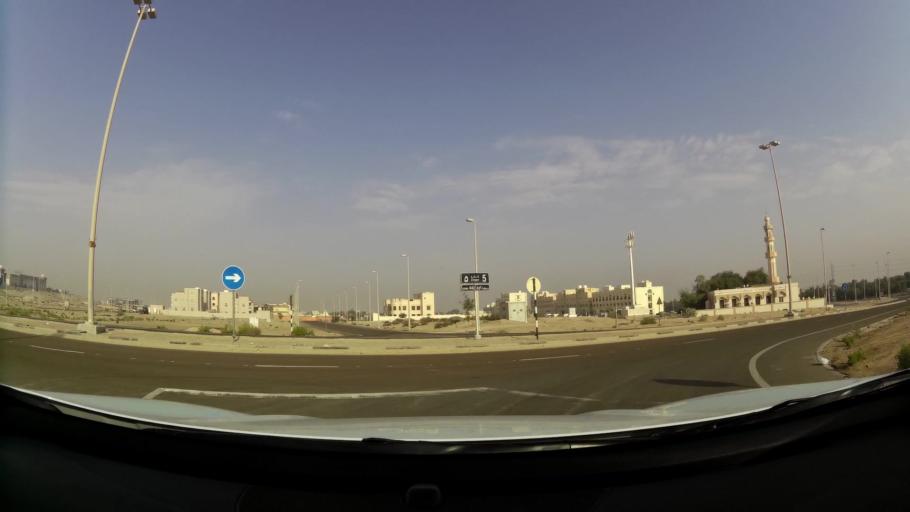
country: AE
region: Abu Dhabi
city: Abu Dhabi
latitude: 24.2716
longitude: 54.6562
